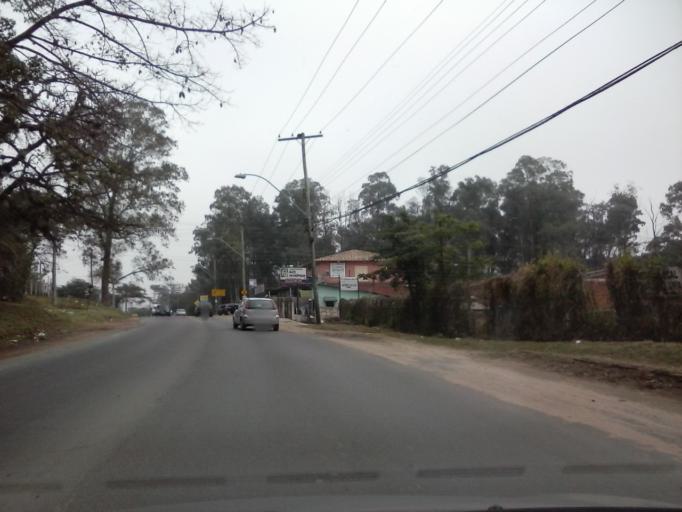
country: BR
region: Rio Grande do Sul
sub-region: Cachoeirinha
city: Cachoeirinha
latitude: -30.0380
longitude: -51.1181
